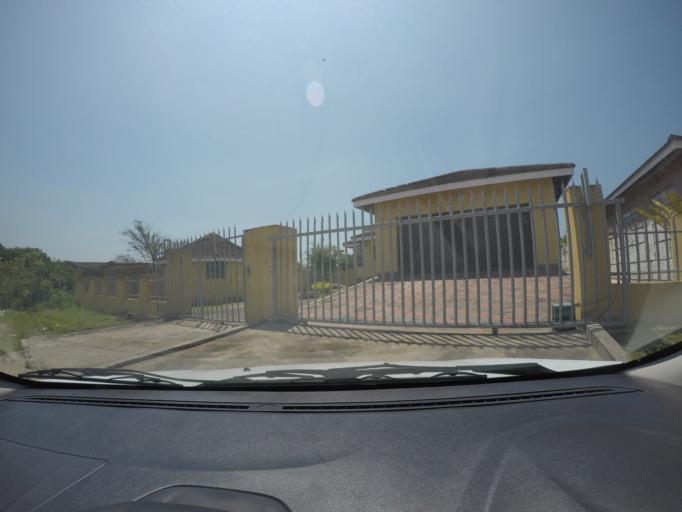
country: ZA
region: KwaZulu-Natal
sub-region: uThungulu District Municipality
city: eSikhawini
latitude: -28.8666
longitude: 31.9214
